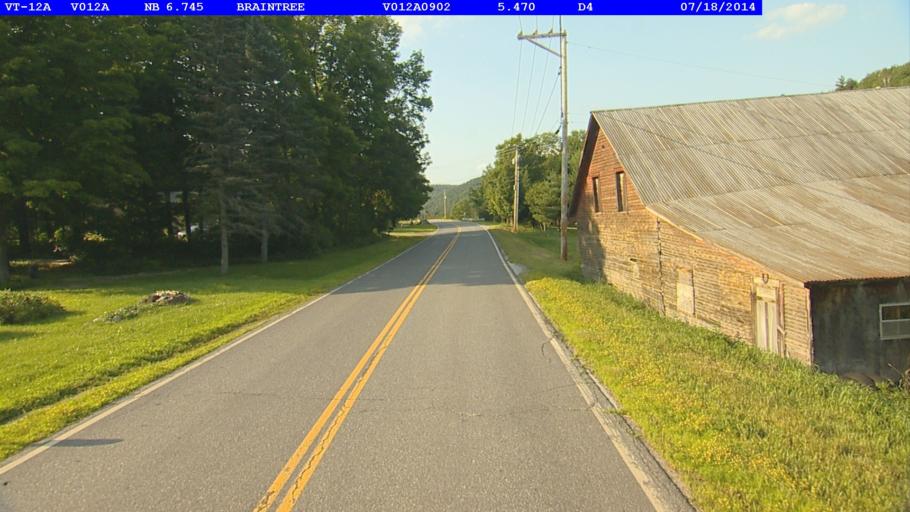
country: US
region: Vermont
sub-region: Orange County
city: Randolph
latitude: 43.9861
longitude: -72.7527
